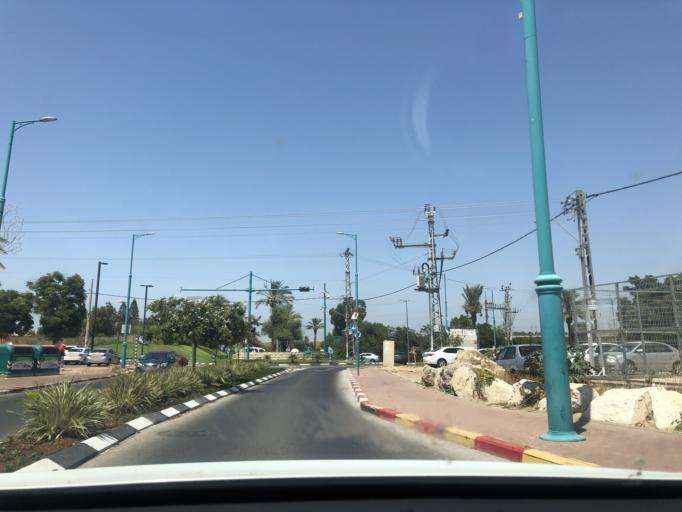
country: IL
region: Central District
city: Lod
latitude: 31.9543
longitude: 34.9043
